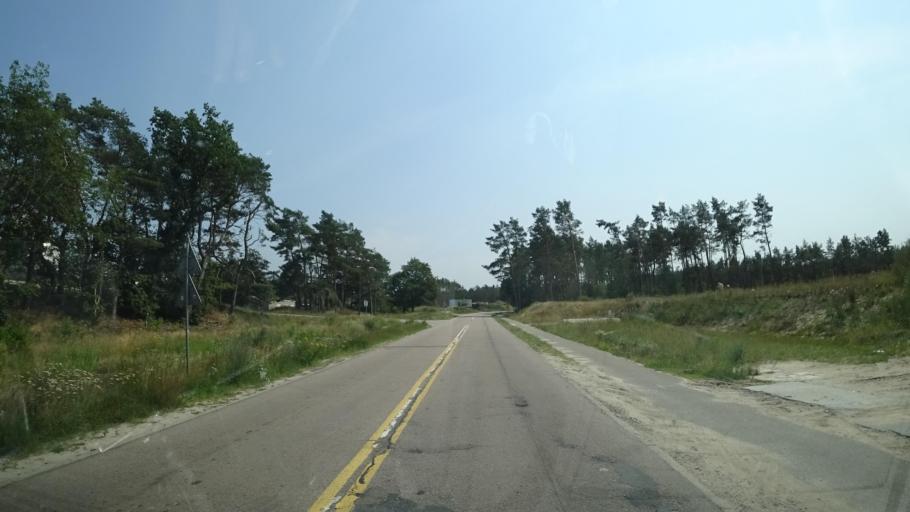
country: PL
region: West Pomeranian Voivodeship
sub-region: Swinoujscie
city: Swinoujscie
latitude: 53.8917
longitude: 14.2428
